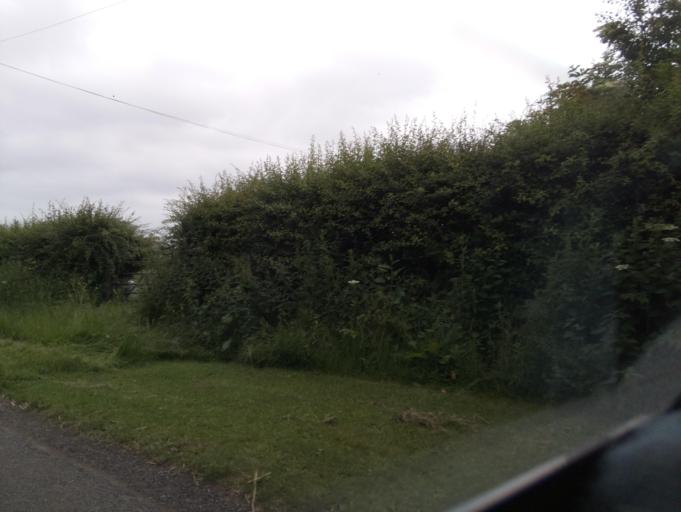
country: GB
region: England
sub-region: Leicestershire
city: Melton Mowbray
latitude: 52.7138
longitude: -0.8311
